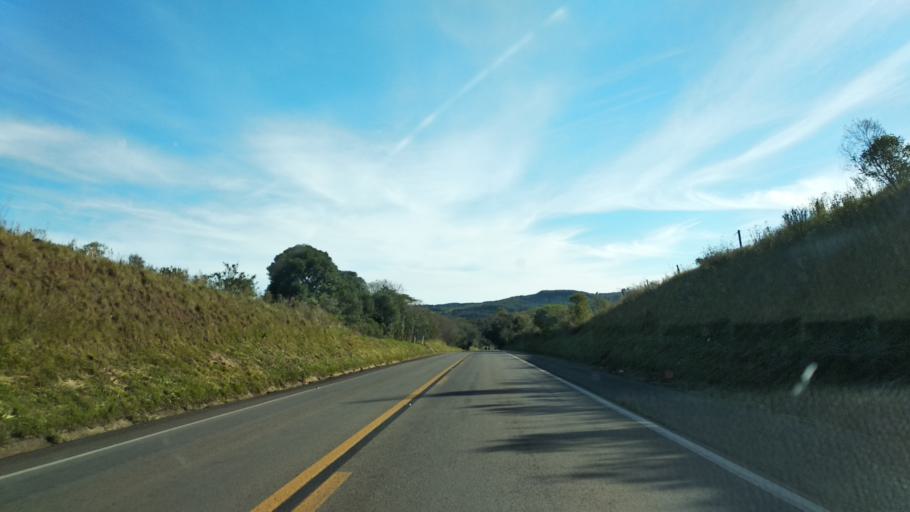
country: BR
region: Santa Catarina
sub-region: Celso Ramos
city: Celso Ramos
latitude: -27.5470
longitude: -51.4317
